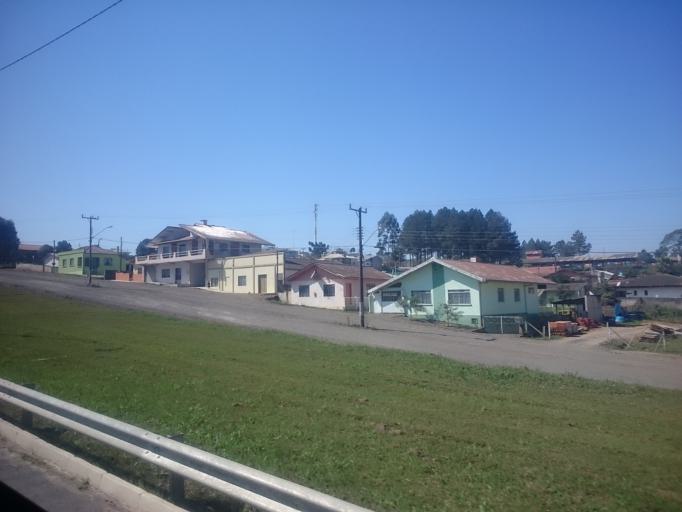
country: BR
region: Santa Catarina
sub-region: Canoinhas
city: Canoinhas
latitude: -26.4591
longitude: -50.2283
